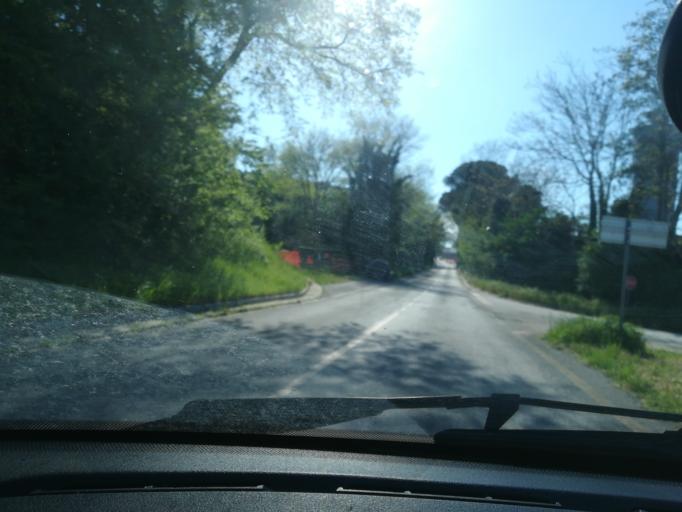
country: IT
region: The Marches
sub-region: Provincia di Macerata
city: Zona Industriale
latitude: 43.2693
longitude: 13.4889
